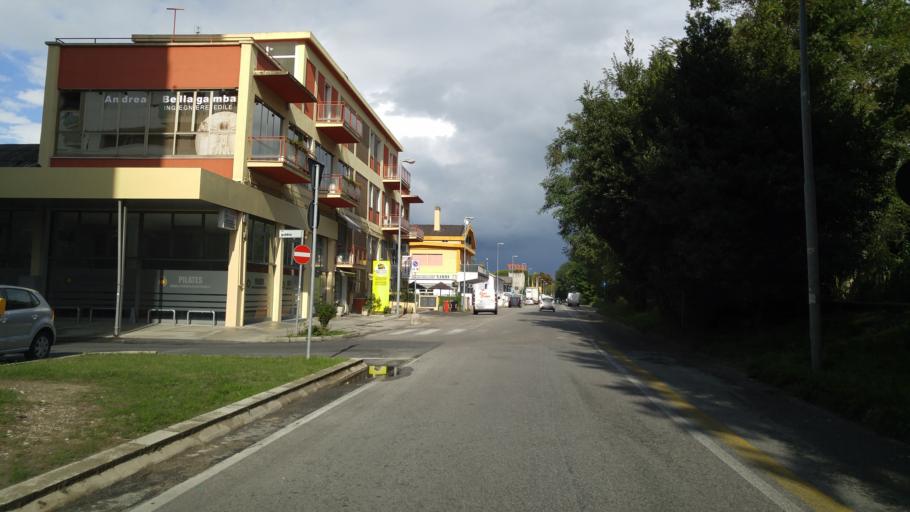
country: IT
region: The Marches
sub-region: Provincia di Pesaro e Urbino
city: Pesaro
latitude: 43.9047
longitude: 12.8919
